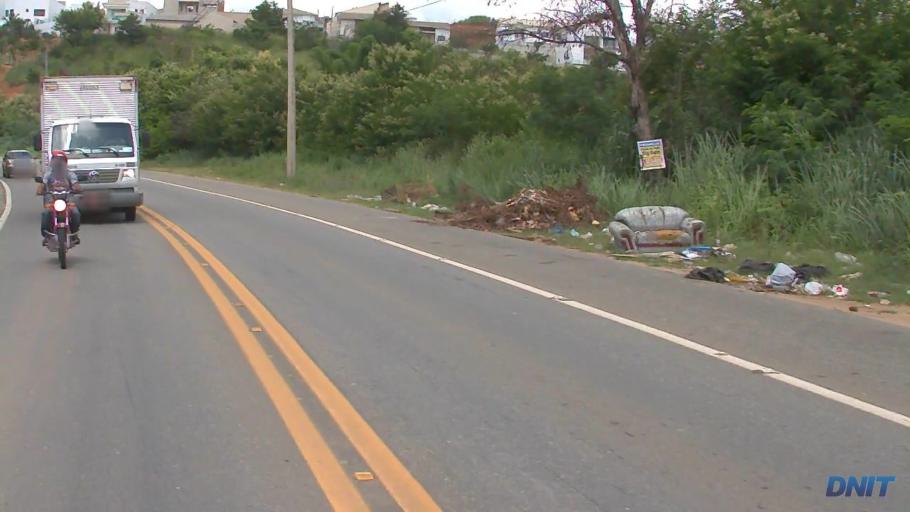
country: BR
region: Minas Gerais
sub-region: Governador Valadares
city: Governador Valadares
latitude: -18.8691
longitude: -41.9907
